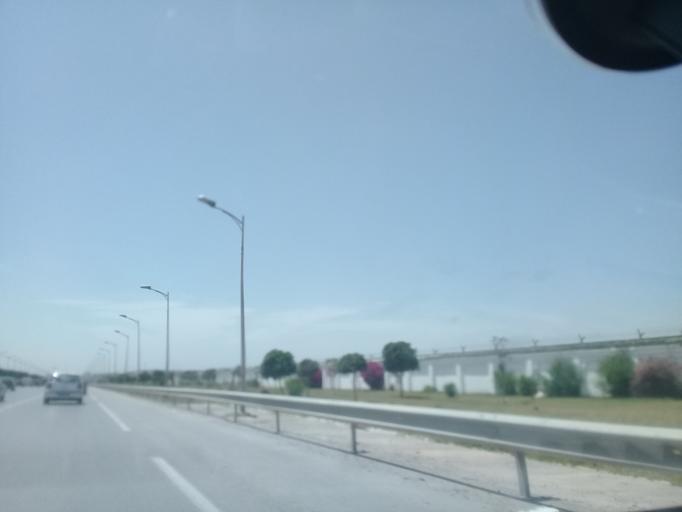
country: TN
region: Ariana
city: Ariana
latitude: 36.8355
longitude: 10.2229
